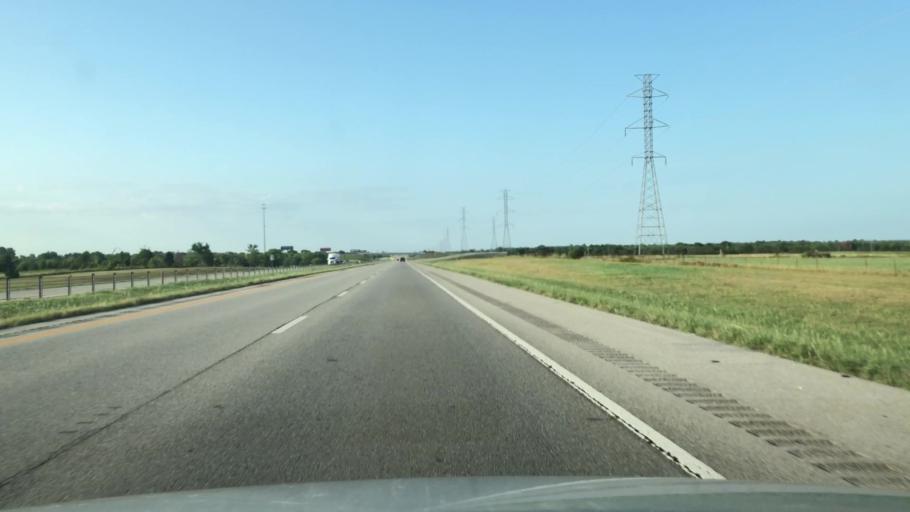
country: US
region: Oklahoma
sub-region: Tulsa County
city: Sperry
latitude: 36.3312
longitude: -95.9243
